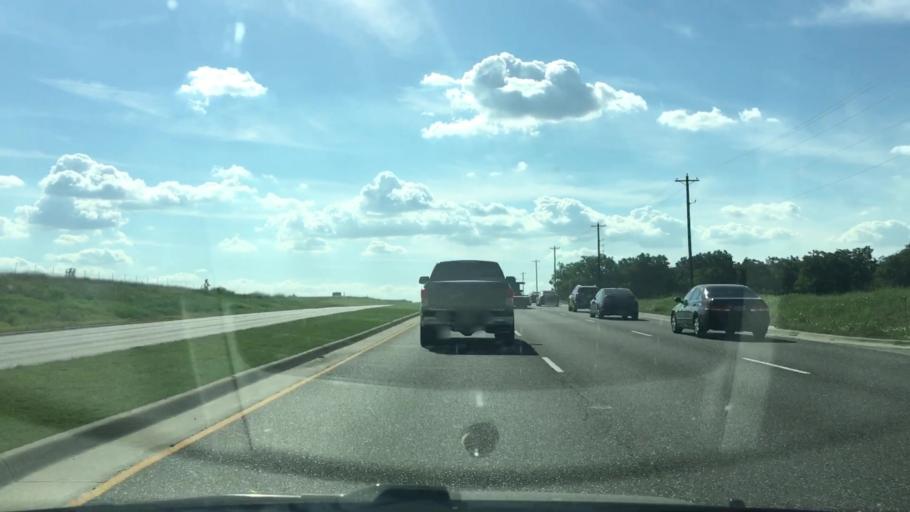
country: US
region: Texas
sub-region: Collin County
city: Prosper
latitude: 33.2190
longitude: -96.7242
